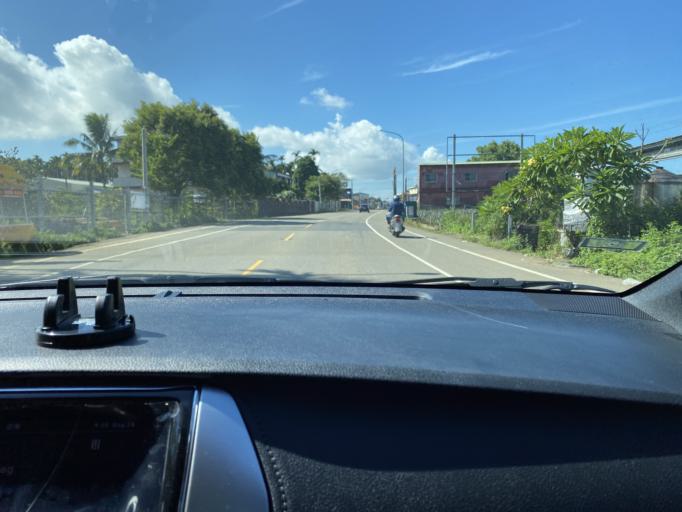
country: TW
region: Taiwan
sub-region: Nantou
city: Nantou
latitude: 23.9212
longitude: 120.6375
